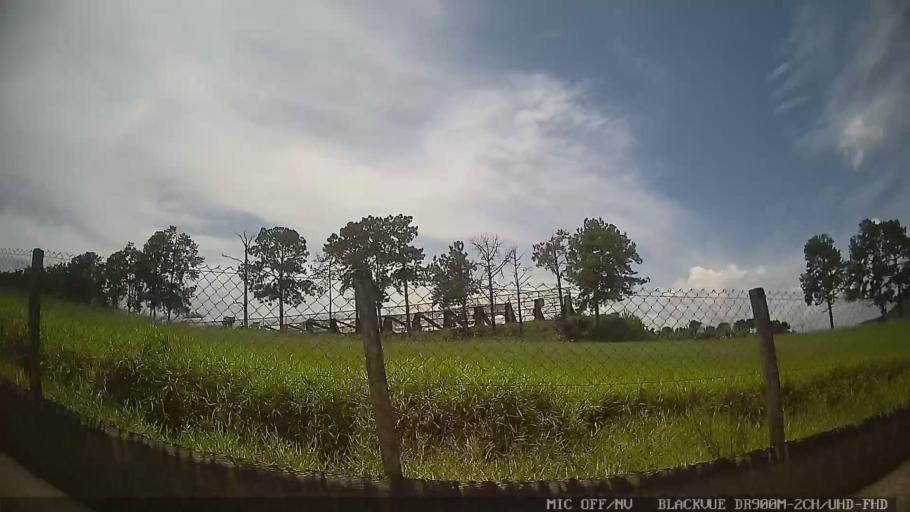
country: BR
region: Sao Paulo
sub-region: Jarinu
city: Jarinu
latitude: -23.0680
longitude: -46.6413
